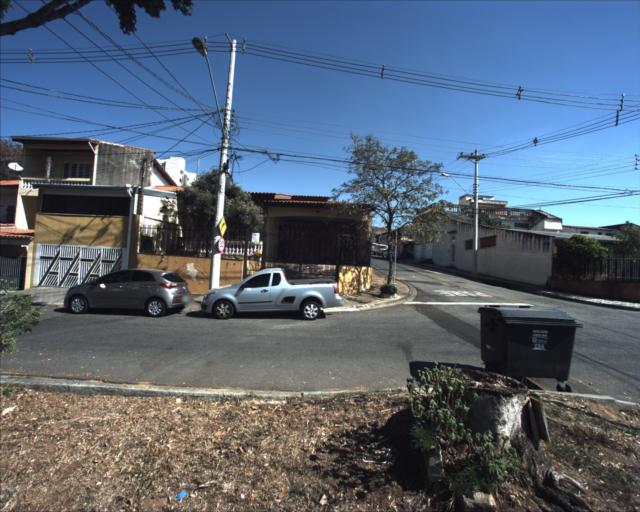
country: BR
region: Sao Paulo
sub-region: Sorocaba
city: Sorocaba
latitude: -23.5035
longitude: -47.4283
